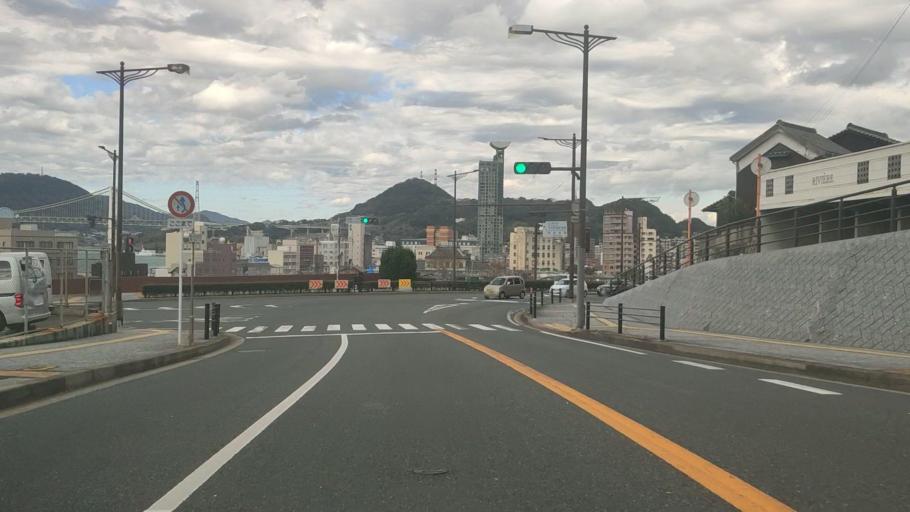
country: JP
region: Yamaguchi
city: Shimonoseki
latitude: 33.9416
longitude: 130.9593
